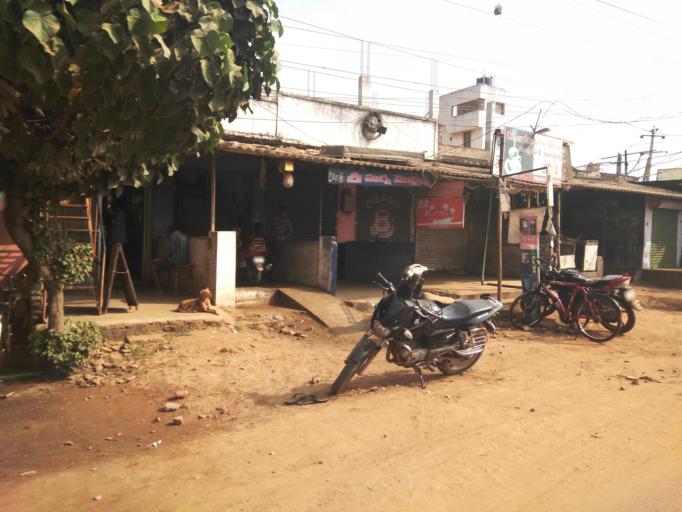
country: IN
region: Andhra Pradesh
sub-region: Nellore
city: Nellore
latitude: 14.4653
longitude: 79.9967
